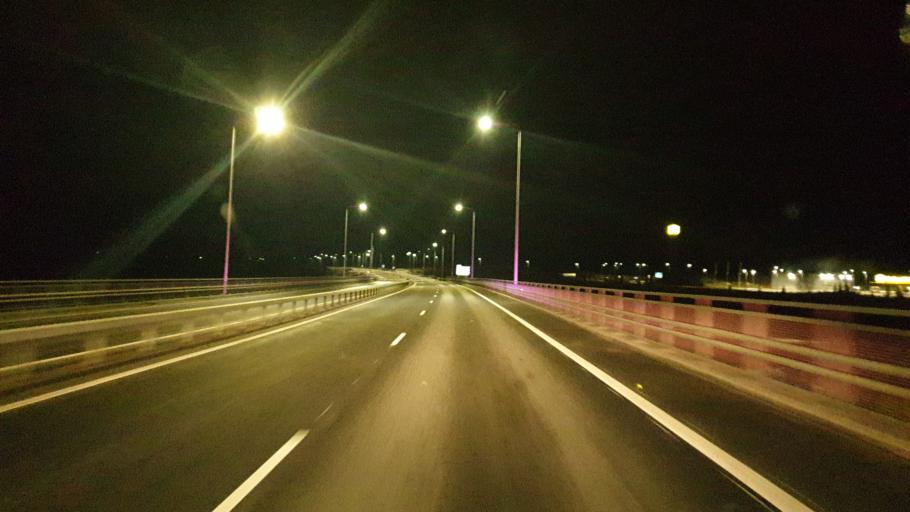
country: FI
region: Central Finland
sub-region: AEaenekoski
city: AEaenekoski
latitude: 62.6043
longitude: 25.6892
